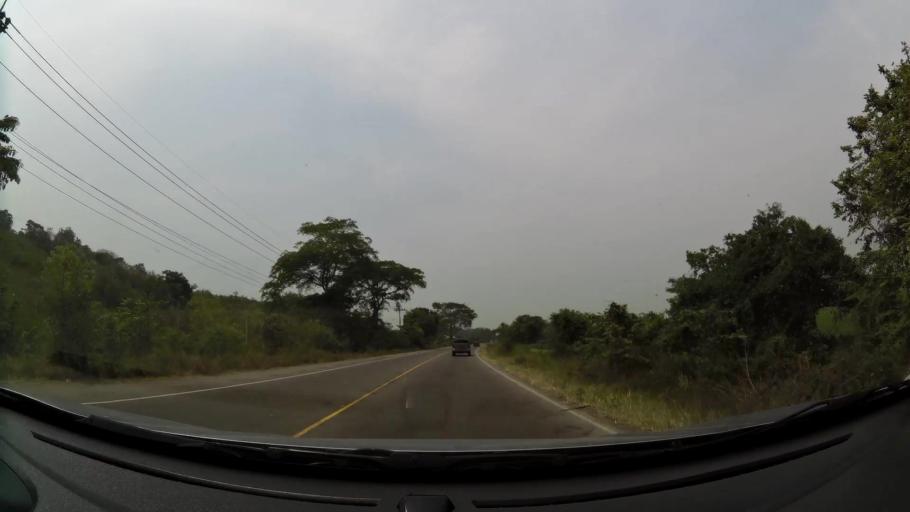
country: HN
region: Cortes
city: Potrerillos
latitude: 15.1811
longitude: -87.9622
